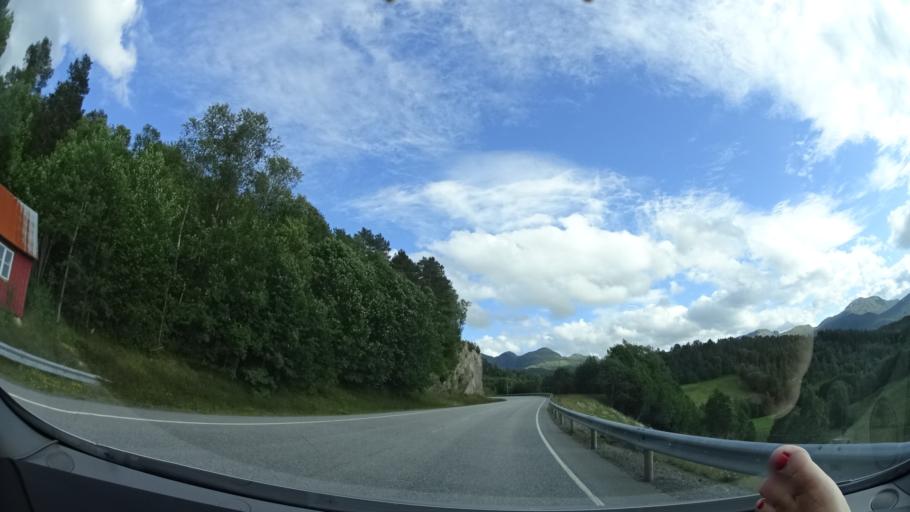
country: NO
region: More og Romsdal
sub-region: Halsa
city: Liaboen
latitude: 63.0997
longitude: 8.3448
